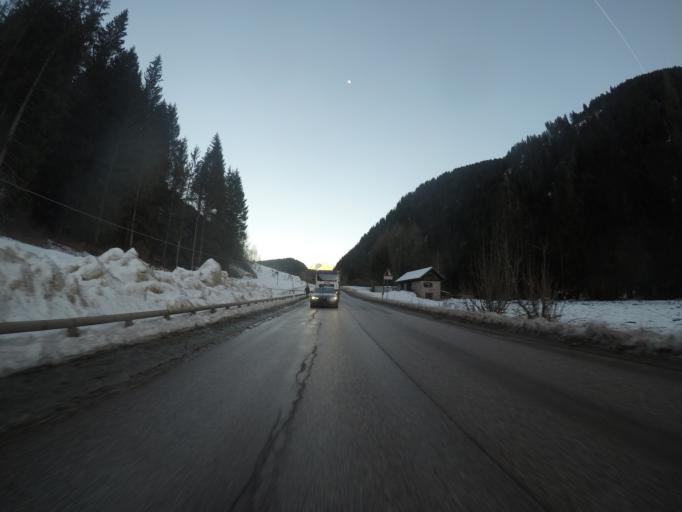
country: IT
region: Trentino-Alto Adige
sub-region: Provincia di Trento
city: Predazzo
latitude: 46.3113
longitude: 11.6183
